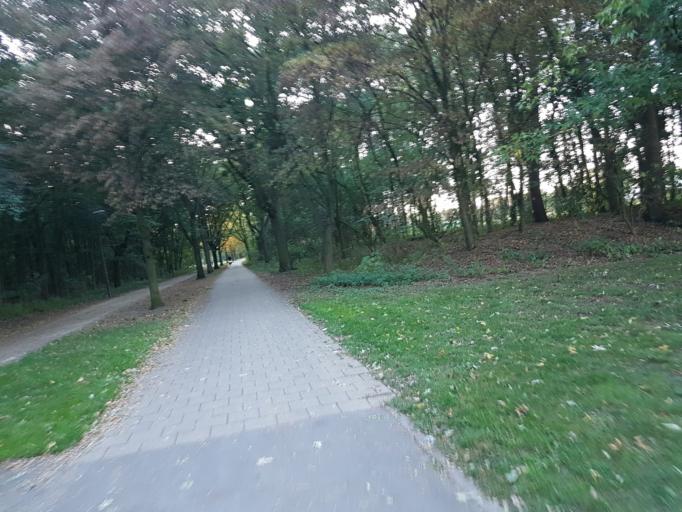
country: DE
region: Lower Saxony
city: Langenhagen
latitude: 52.4459
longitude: 9.7504
